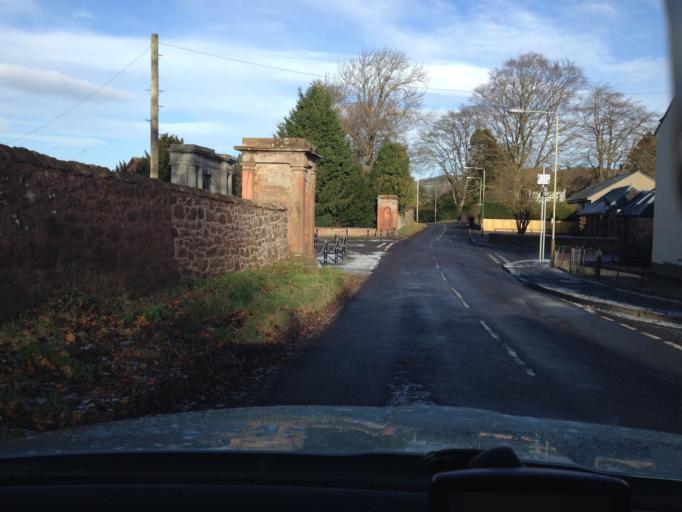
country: GB
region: Scotland
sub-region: Perth and Kinross
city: Bridge of Earn
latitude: 56.3406
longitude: -3.4100
